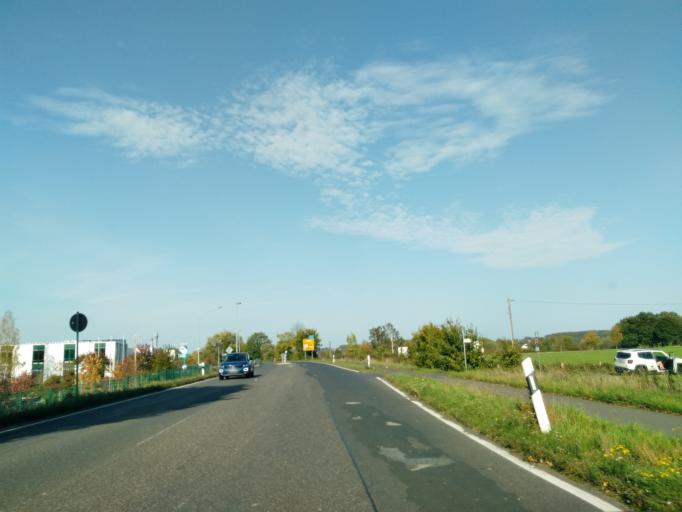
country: DE
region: North Rhine-Westphalia
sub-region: Regierungsbezirk Koln
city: Bad Honnef
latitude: 50.6950
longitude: 7.2784
